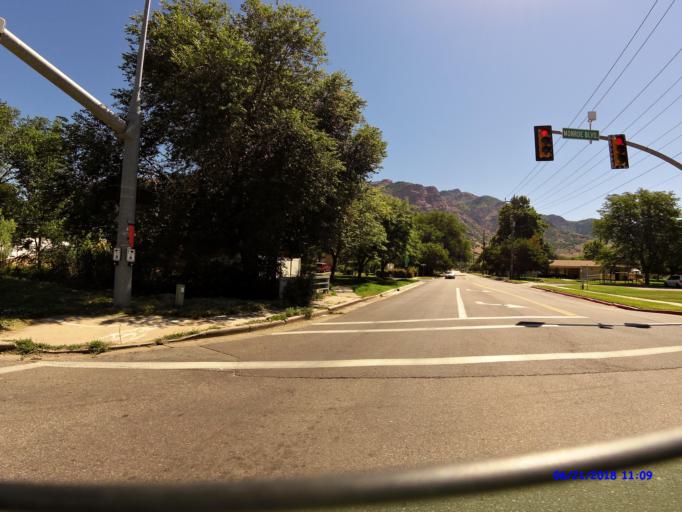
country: US
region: Utah
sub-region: Weber County
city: Harrisville
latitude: 41.2590
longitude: -111.9561
